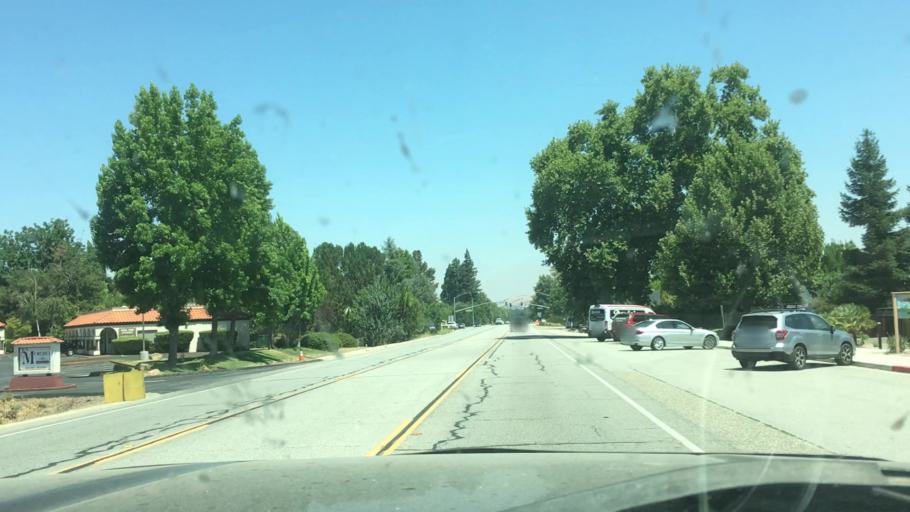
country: US
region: California
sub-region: San Luis Obispo County
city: Atascadero
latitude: 35.4718
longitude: -120.6690
